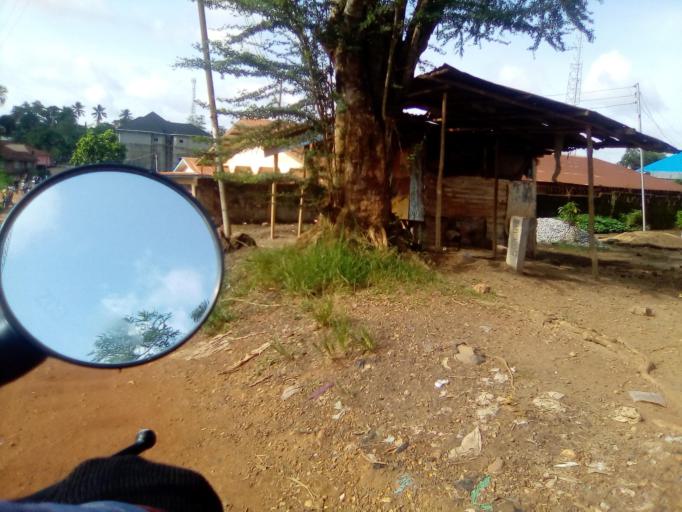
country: SL
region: Southern Province
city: Bo
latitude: 7.9709
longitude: -11.7312
